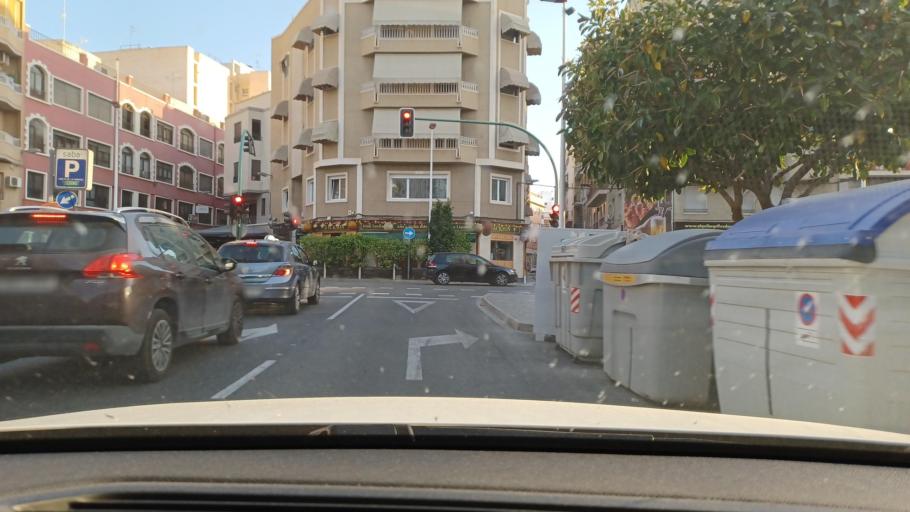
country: ES
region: Valencia
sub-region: Provincia de Alicante
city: Elche
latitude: 38.2640
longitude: -0.6948
